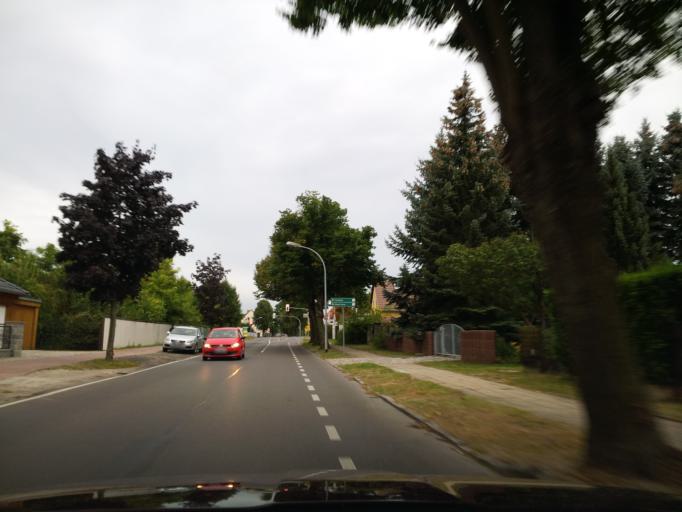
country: DE
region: Brandenburg
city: Luckenwalde
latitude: 52.0970
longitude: 13.1523
